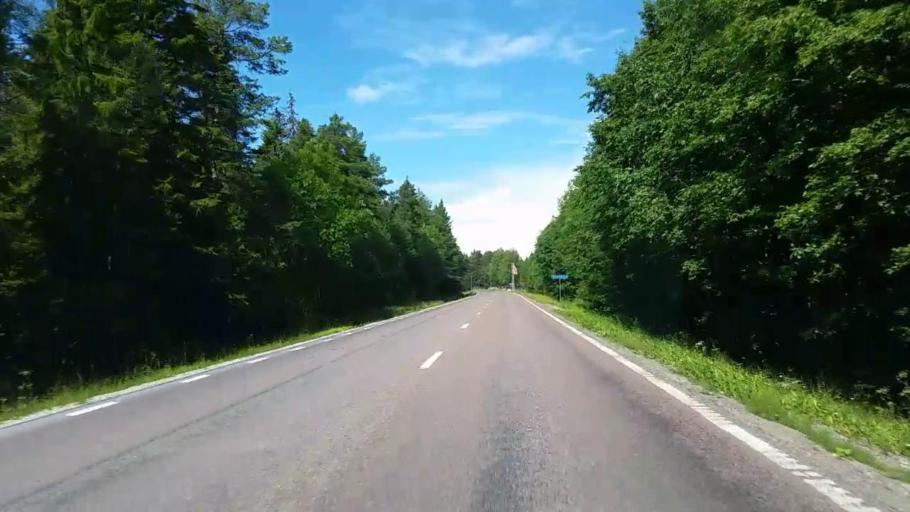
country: SE
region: Dalarna
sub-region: Rattviks Kommun
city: Raettvik
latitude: 61.0329
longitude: 15.2047
